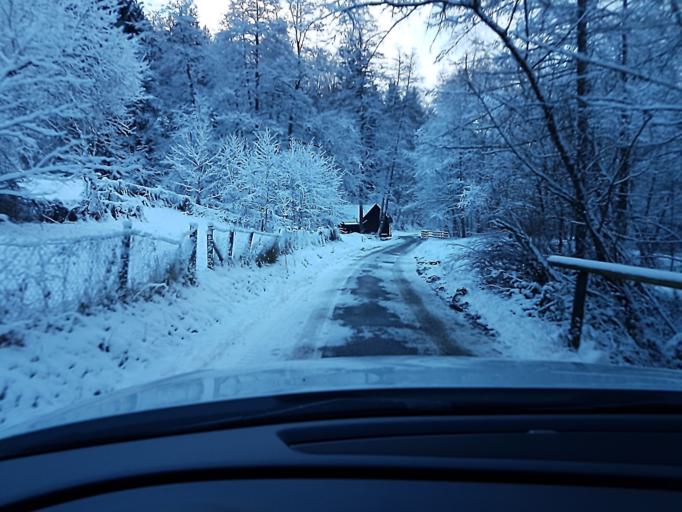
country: DE
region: Baden-Wuerttemberg
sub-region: Regierungsbezirk Stuttgart
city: Fichtenberg
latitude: 48.9639
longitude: 9.6927
